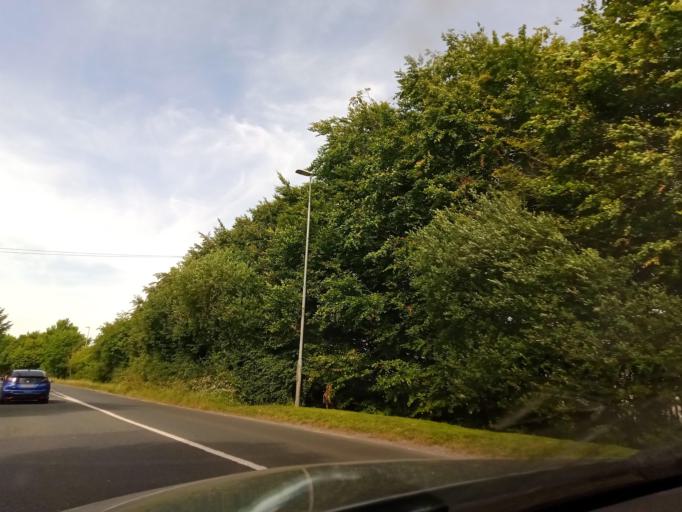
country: IE
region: Leinster
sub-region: Laois
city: Portlaoise
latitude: 53.0215
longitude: -7.2998
